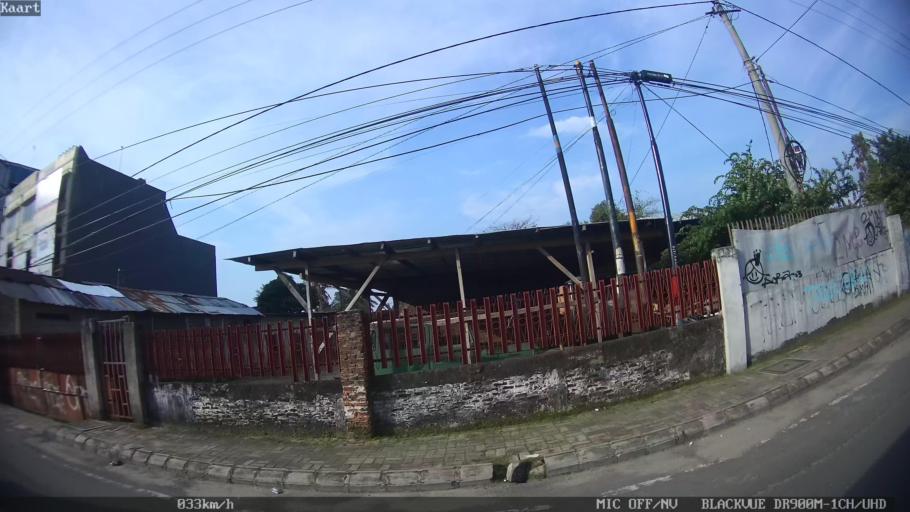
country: ID
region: Lampung
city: Kedaton
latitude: -5.3809
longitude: 105.2558
